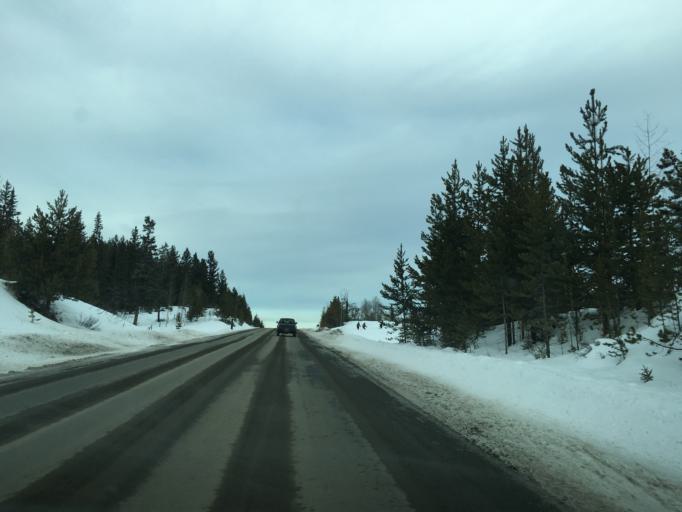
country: CA
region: British Columbia
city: Kamloops
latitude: 50.5348
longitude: -120.4507
